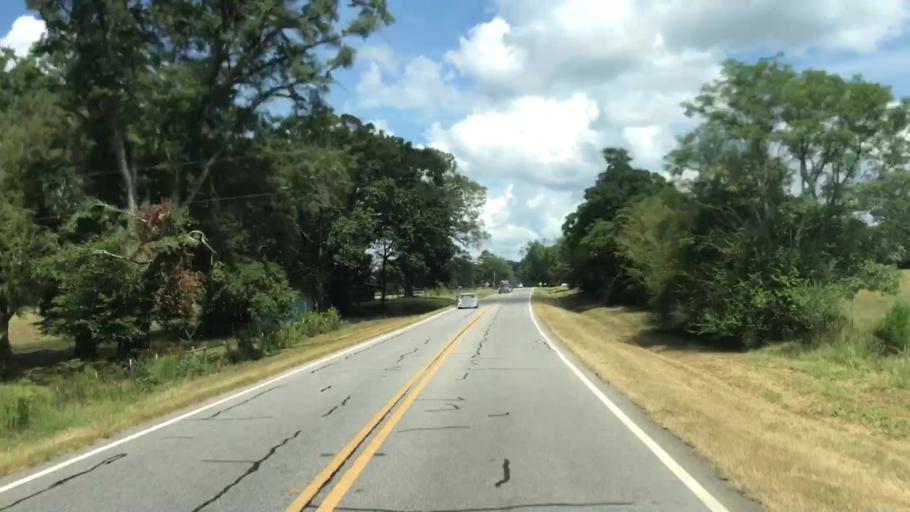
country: US
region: Georgia
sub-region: Oconee County
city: Watkinsville
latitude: 33.7413
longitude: -83.3030
